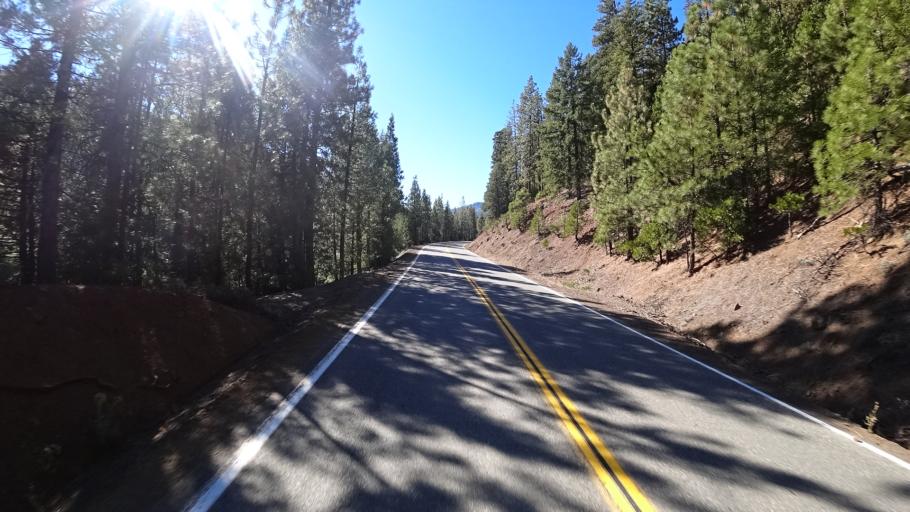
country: US
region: California
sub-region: Siskiyou County
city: Weed
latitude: 41.2705
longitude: -122.8797
